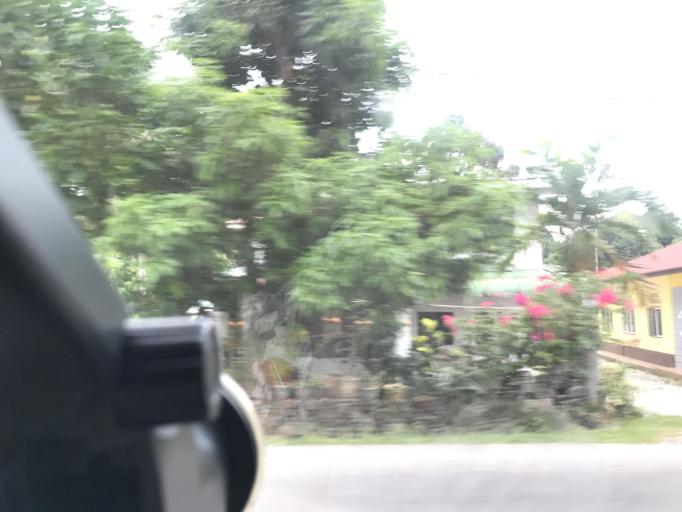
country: MY
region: Kelantan
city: Kota Bharu
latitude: 6.1244
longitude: 102.1746
